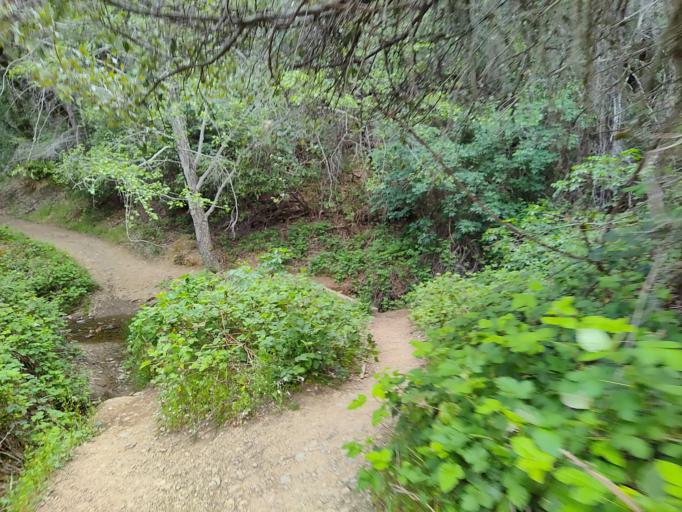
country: US
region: California
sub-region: Placer County
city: Colfax
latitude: 39.1126
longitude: -120.9410
